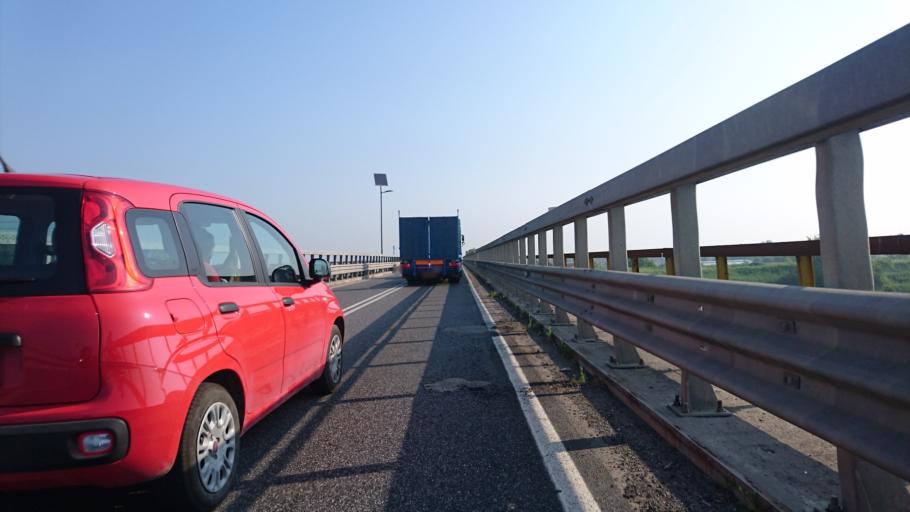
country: IT
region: Veneto
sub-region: Provincia di Rovigo
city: Castelnovo Bariano
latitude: 45.0200
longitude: 11.2921
